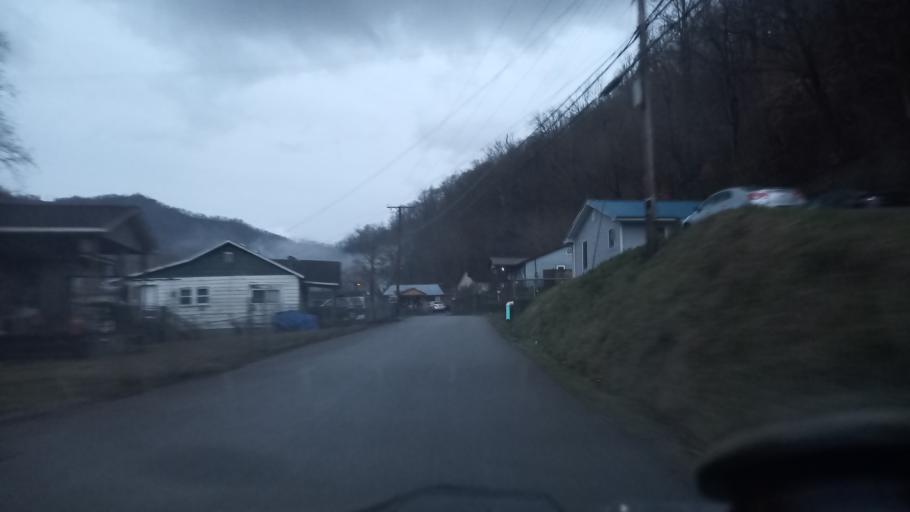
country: US
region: West Virginia
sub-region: Logan County
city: Mallory
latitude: 37.7256
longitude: -81.8765
